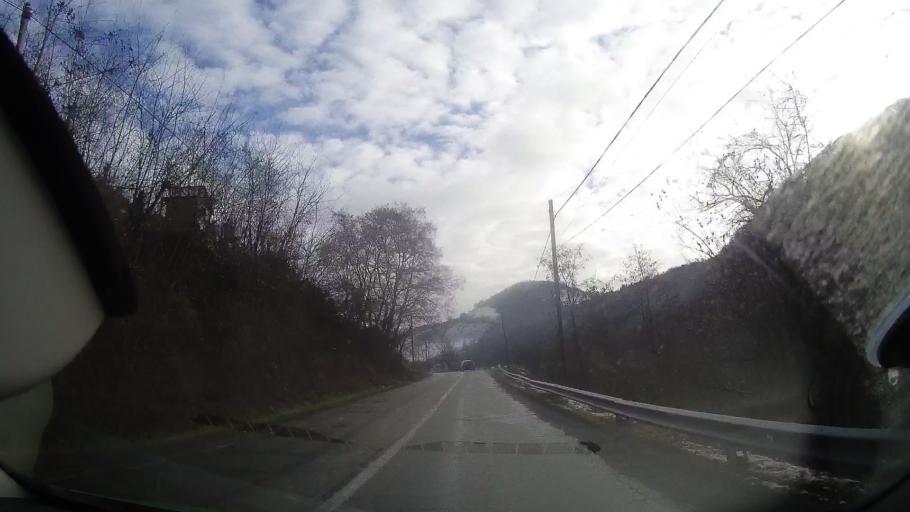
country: RO
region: Alba
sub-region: Oras Baia de Aries
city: Baia de Aries
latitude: 46.3749
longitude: 23.2521
